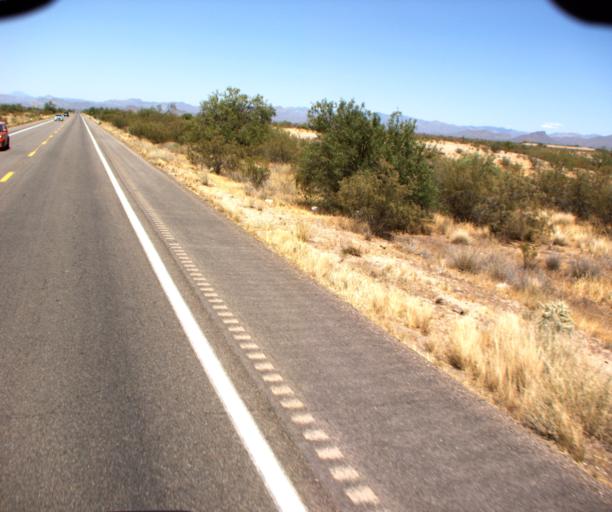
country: US
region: Arizona
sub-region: Pinal County
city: Gold Camp
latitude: 33.1820
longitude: -111.3516
